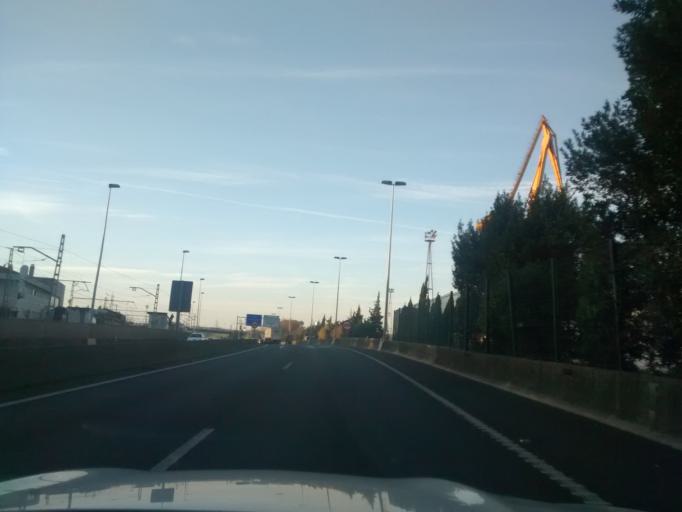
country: ES
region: Cantabria
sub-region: Provincia de Cantabria
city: El Astillero
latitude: 43.4033
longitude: -3.8188
